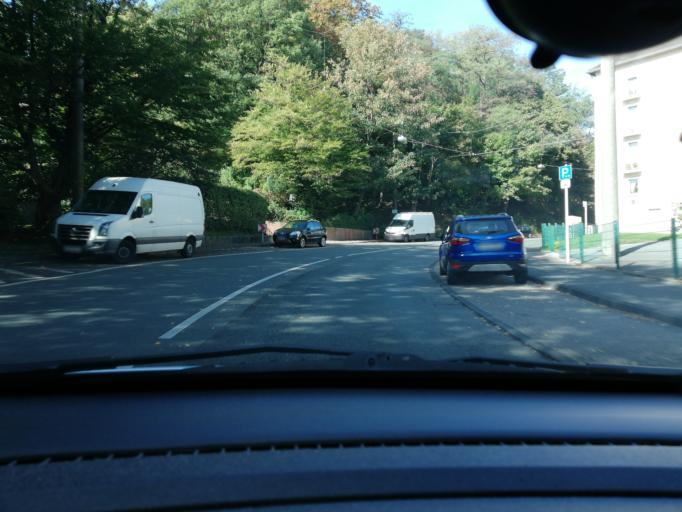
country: DE
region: North Rhine-Westphalia
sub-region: Regierungsbezirk Dusseldorf
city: Wuppertal
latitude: 51.2856
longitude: 7.2064
